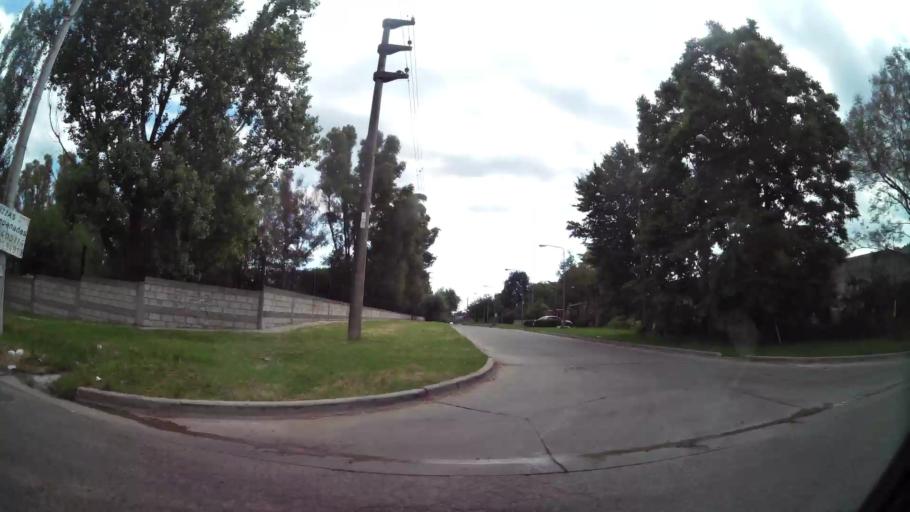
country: AR
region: Buenos Aires
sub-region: Partido de Tigre
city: Tigre
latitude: -34.4781
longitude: -58.6413
